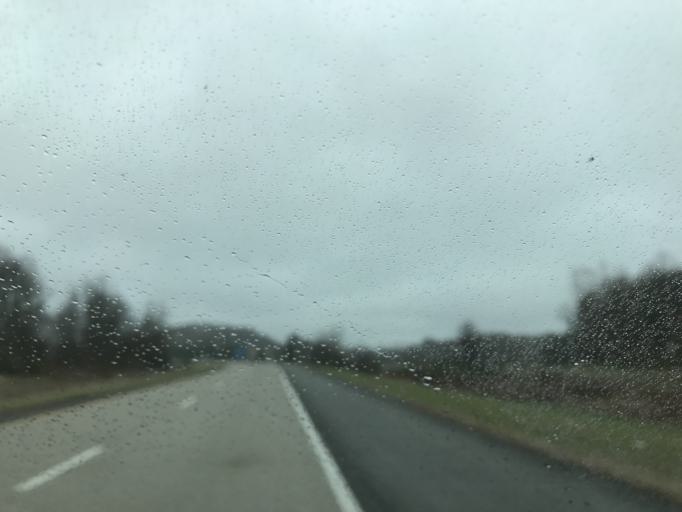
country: US
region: West Virginia
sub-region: Greenbrier County
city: Rainelle
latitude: 37.8420
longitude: -80.7370
